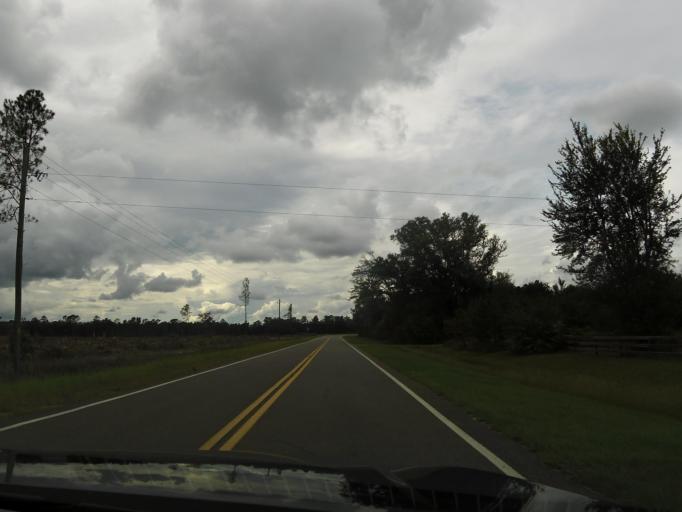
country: US
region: Florida
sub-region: Baker County
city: Macclenny
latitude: 30.5114
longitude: -82.2196
